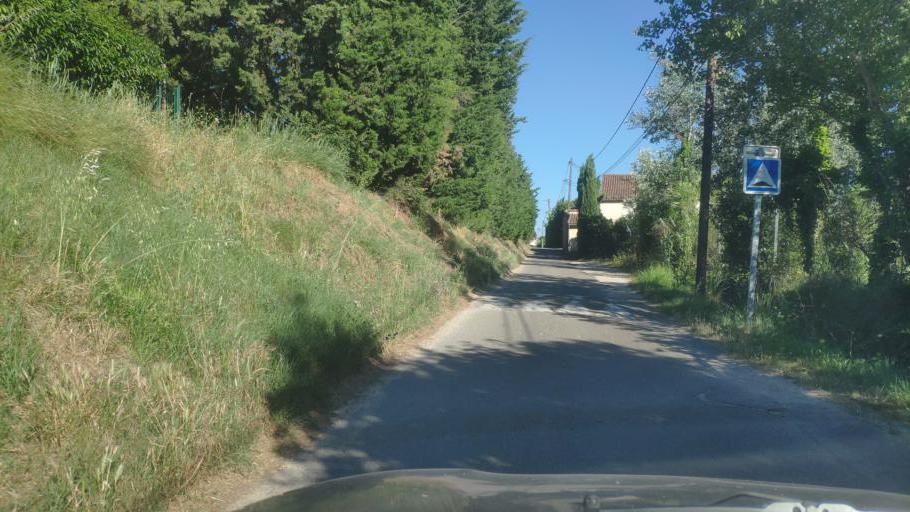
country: FR
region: Provence-Alpes-Cote d'Azur
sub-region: Departement du Vaucluse
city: Aubignan
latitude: 44.0926
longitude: 5.0340
